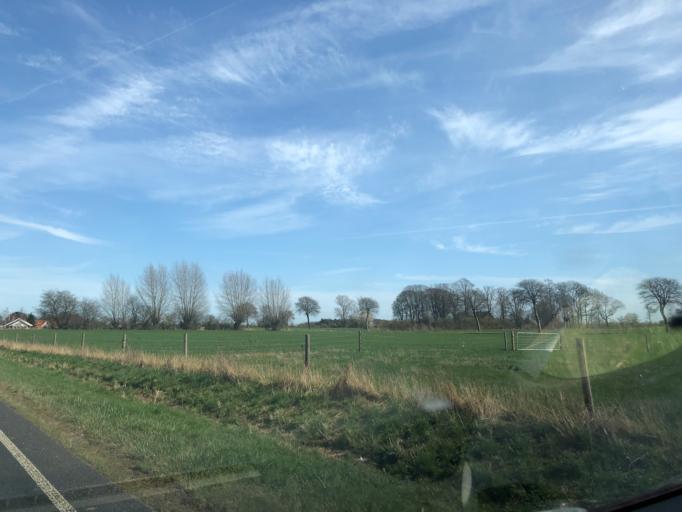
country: DK
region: Zealand
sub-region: Stevns Kommune
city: Store Heddinge
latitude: 55.2807
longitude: 12.3049
